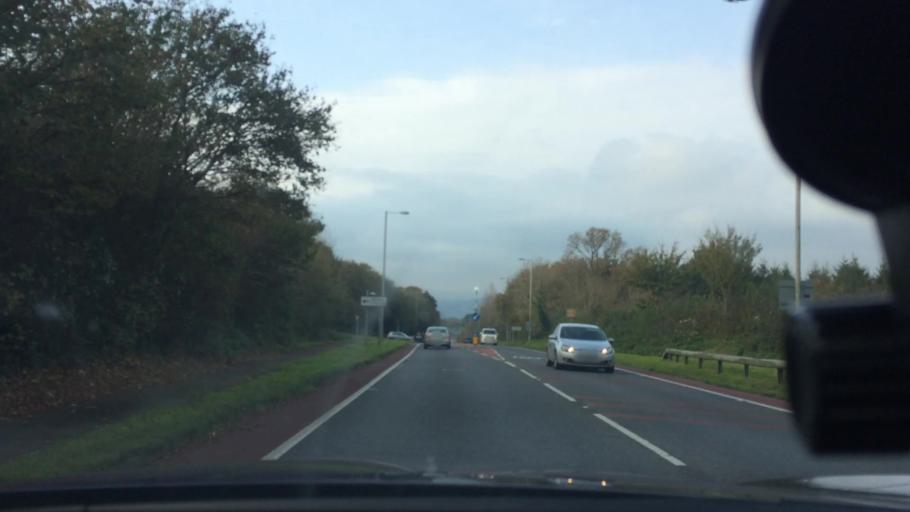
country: GB
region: England
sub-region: Devon
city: Axminster
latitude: 50.7632
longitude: -2.9706
